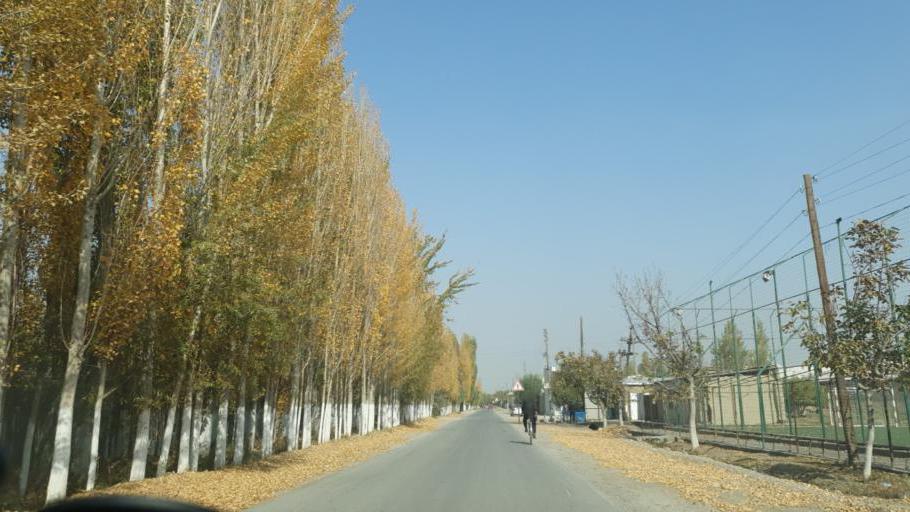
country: UZ
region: Fergana
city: Beshariq
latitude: 40.4915
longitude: 70.6209
